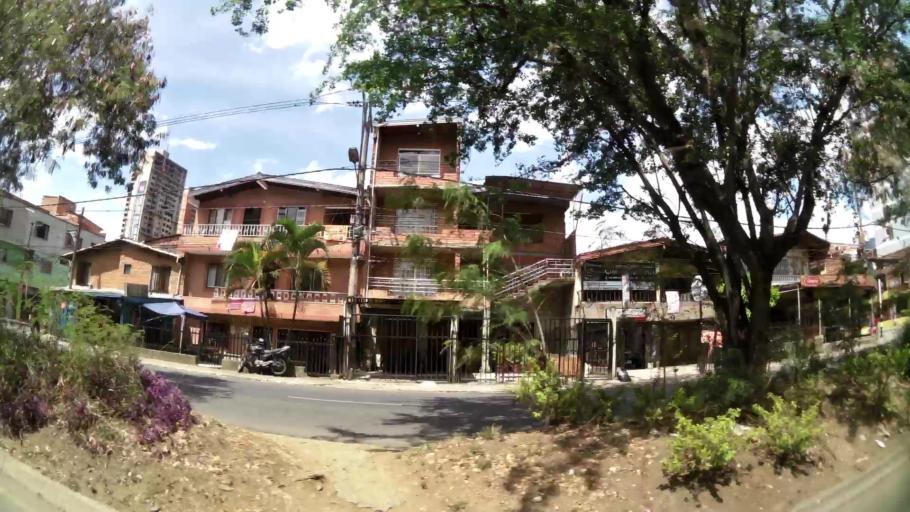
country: CO
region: Antioquia
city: Bello
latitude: 6.3387
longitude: -75.5481
